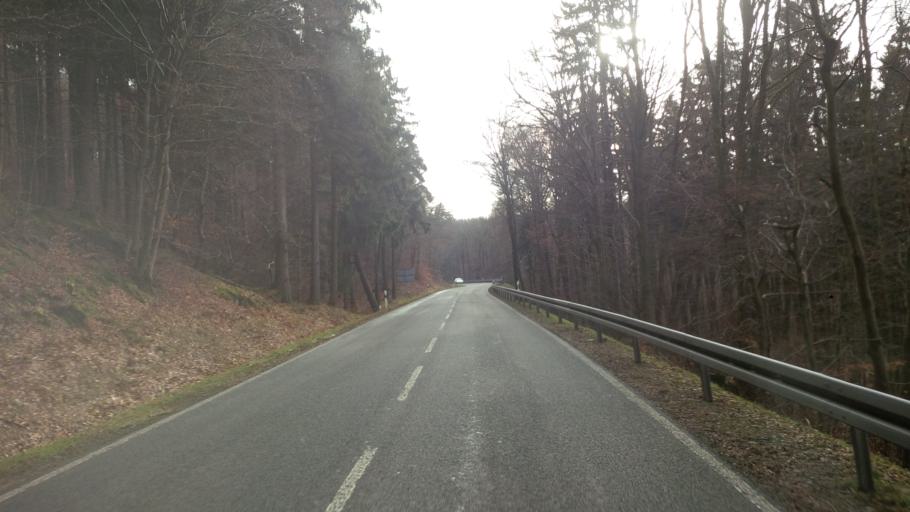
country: DE
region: Hesse
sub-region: Regierungsbezirk Darmstadt
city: Schmitten
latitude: 50.2629
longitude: 8.4614
